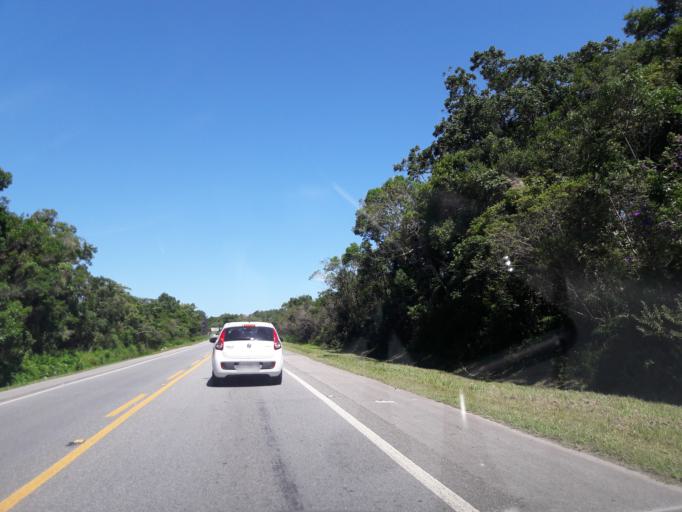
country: BR
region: Parana
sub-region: Pontal Do Parana
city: Pontal do Parana
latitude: -25.6681
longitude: -48.5165
